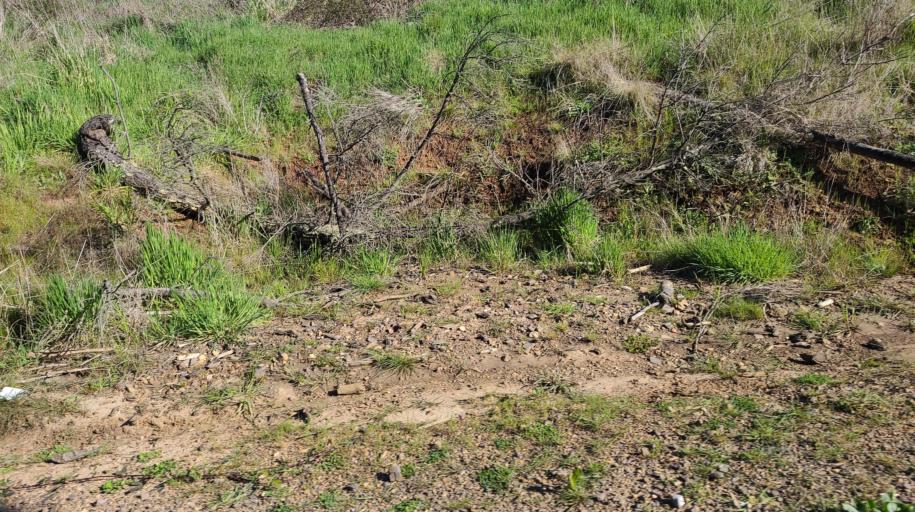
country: AU
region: New South Wales
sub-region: Blayney
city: Blayney
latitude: -33.4137
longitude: 149.3200
